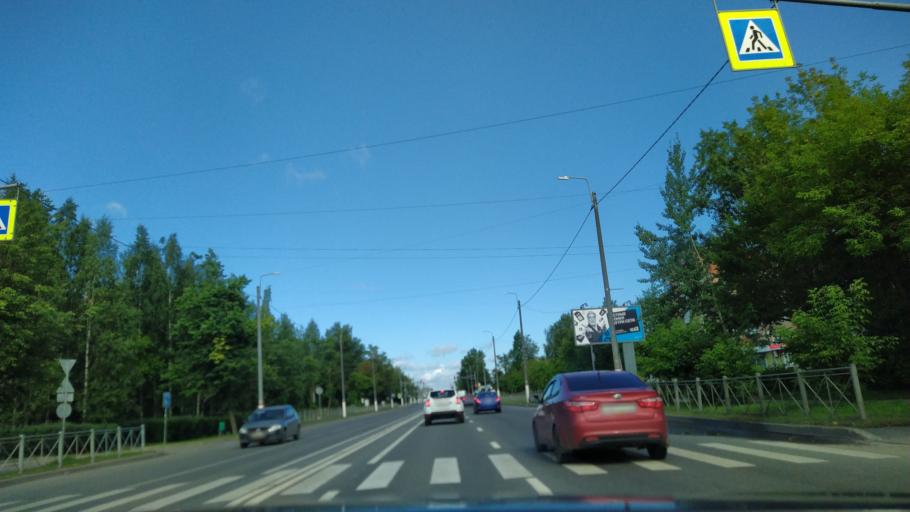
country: RU
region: Leningrad
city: Tosno
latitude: 59.5465
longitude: 30.8671
